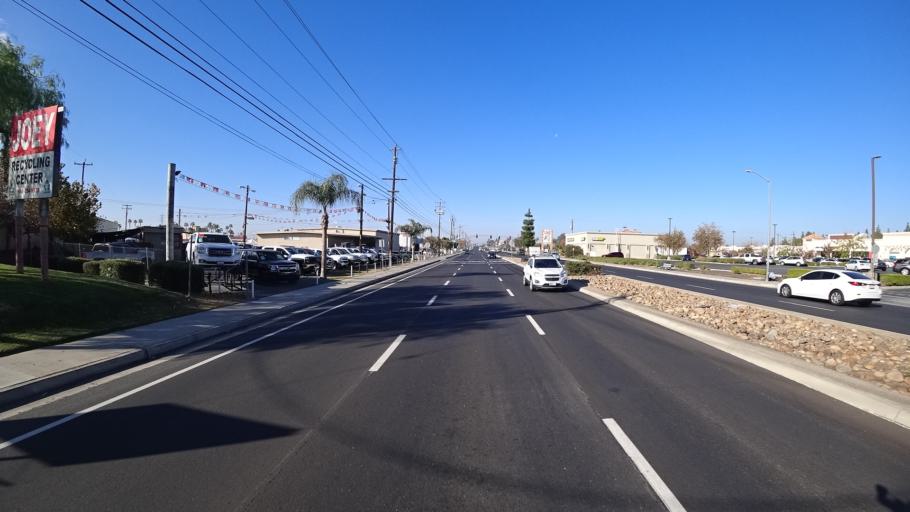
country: US
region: California
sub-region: Kern County
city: Greenfield
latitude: 35.3176
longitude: -119.0265
